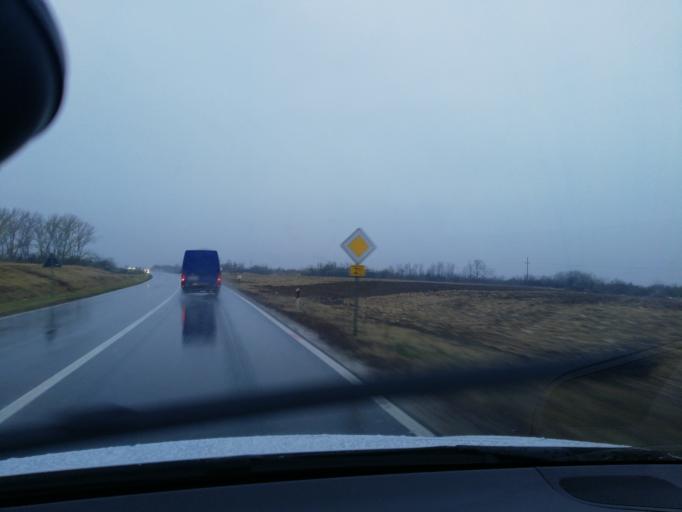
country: RS
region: Autonomna Pokrajina Vojvodina
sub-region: Sremski Okrug
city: Ruma
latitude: 45.0230
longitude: 19.8358
